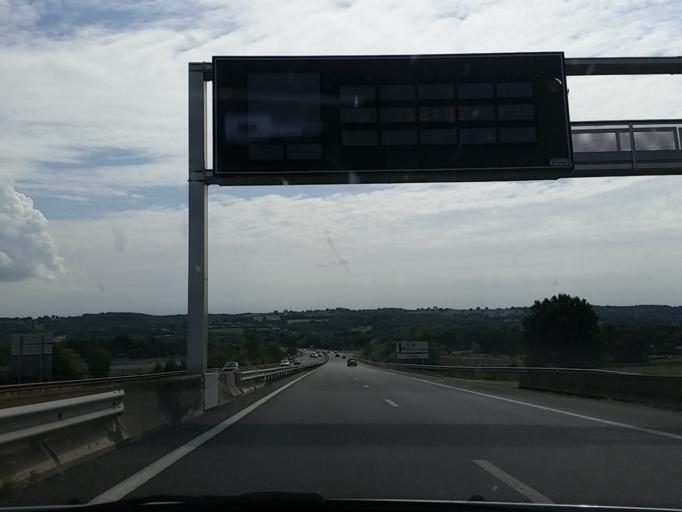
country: FR
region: Auvergne
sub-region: Departement de l'Allier
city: Vallon-en-Sully
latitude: 46.5110
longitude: 2.6008
